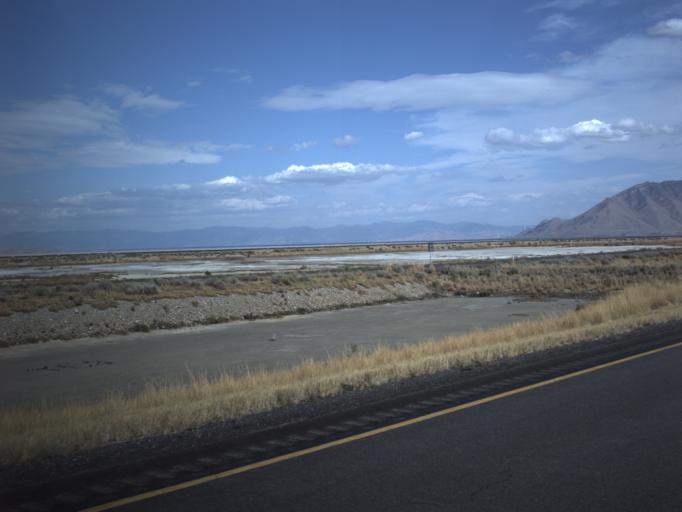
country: US
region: Utah
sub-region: Tooele County
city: Grantsville
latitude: 40.6830
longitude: -112.4361
